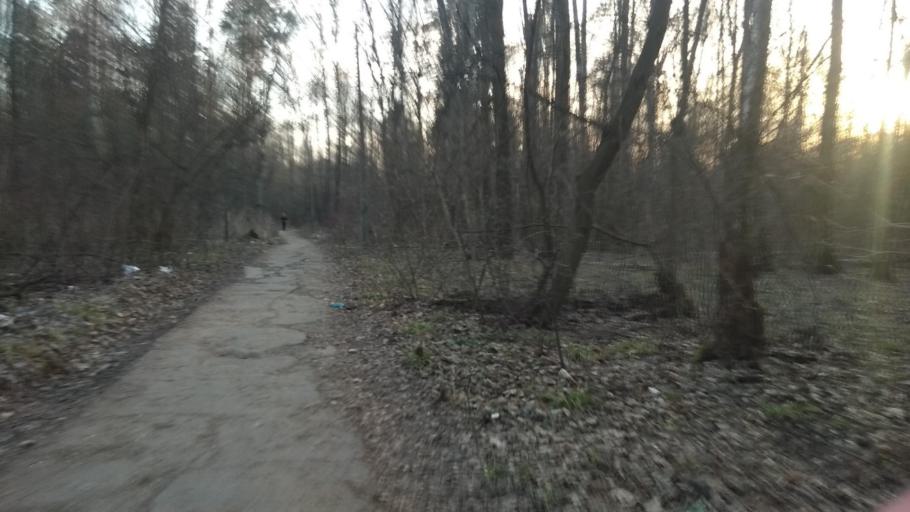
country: RU
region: Moskovskaya
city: Razvilka
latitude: 55.5610
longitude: 37.7438
